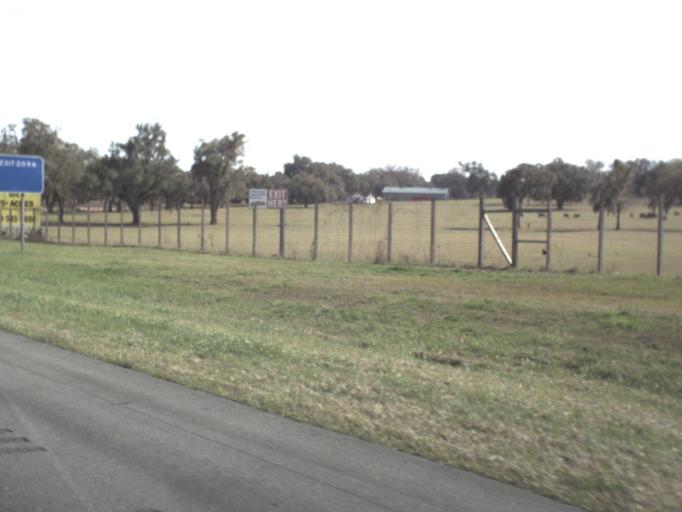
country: US
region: Florida
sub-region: Leon County
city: Tallahassee
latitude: 30.4922
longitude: -84.1693
